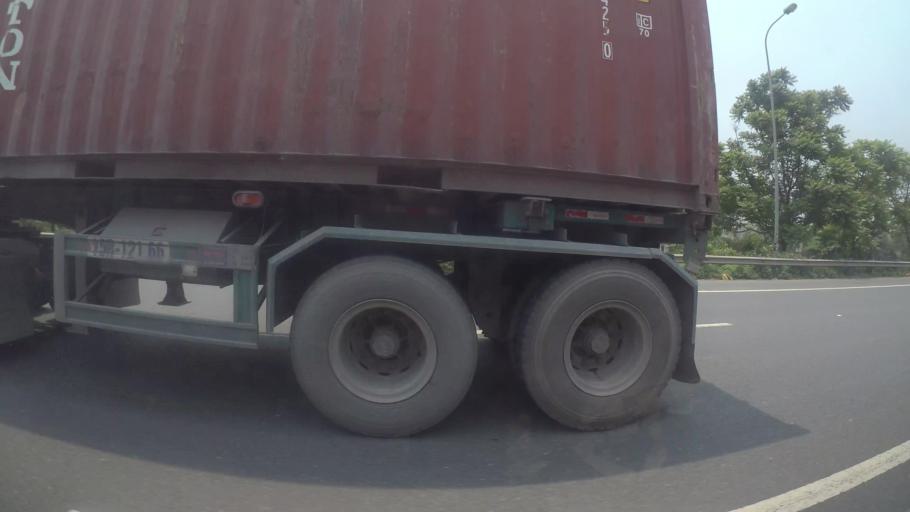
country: VN
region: Ha Noi
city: Cau Dien
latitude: 21.0104
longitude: 105.7315
